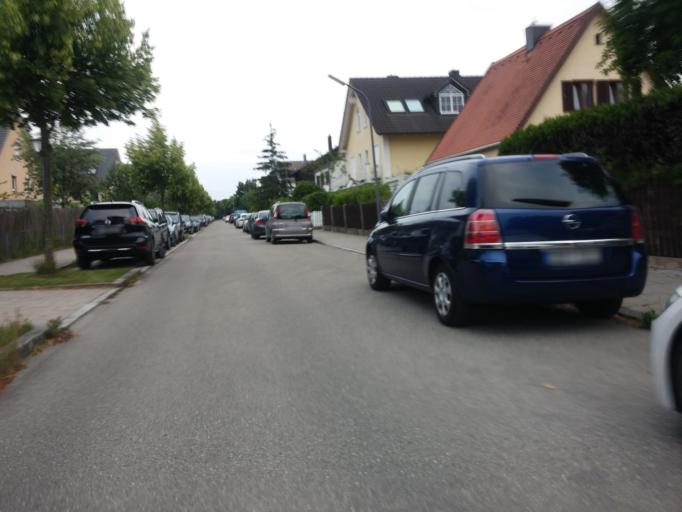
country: DE
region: Bavaria
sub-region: Upper Bavaria
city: Neubiberg
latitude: 48.1179
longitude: 11.6637
